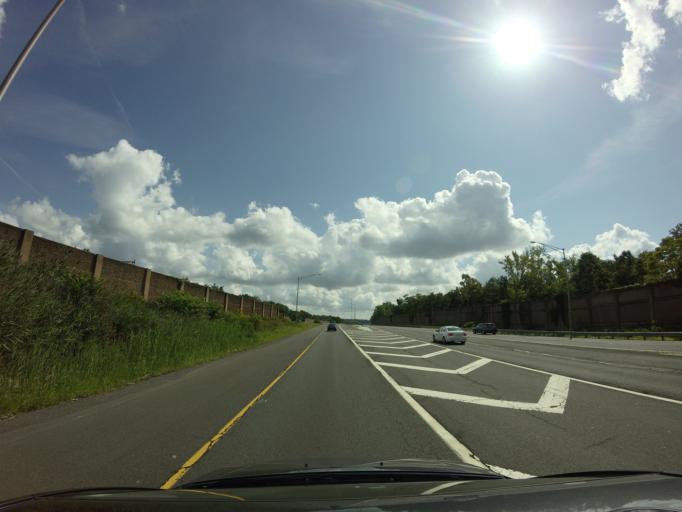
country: US
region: New Jersey
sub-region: Union County
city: Springfield
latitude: 40.7120
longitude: -74.3204
